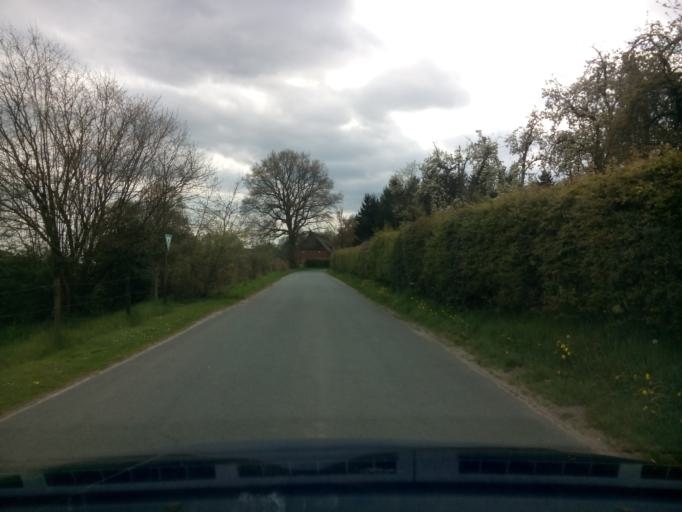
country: DE
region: Lower Saxony
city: Vollersode
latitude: 53.3201
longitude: 8.8881
